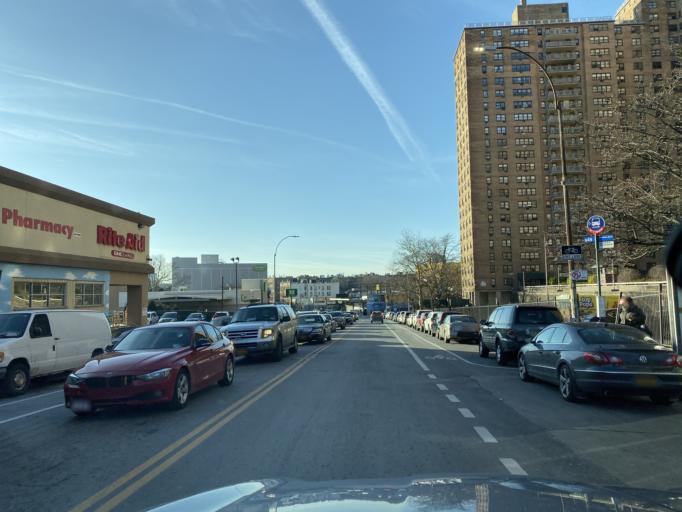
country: US
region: New York
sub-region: Kings County
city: Brooklyn
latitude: 40.6654
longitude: -73.9569
